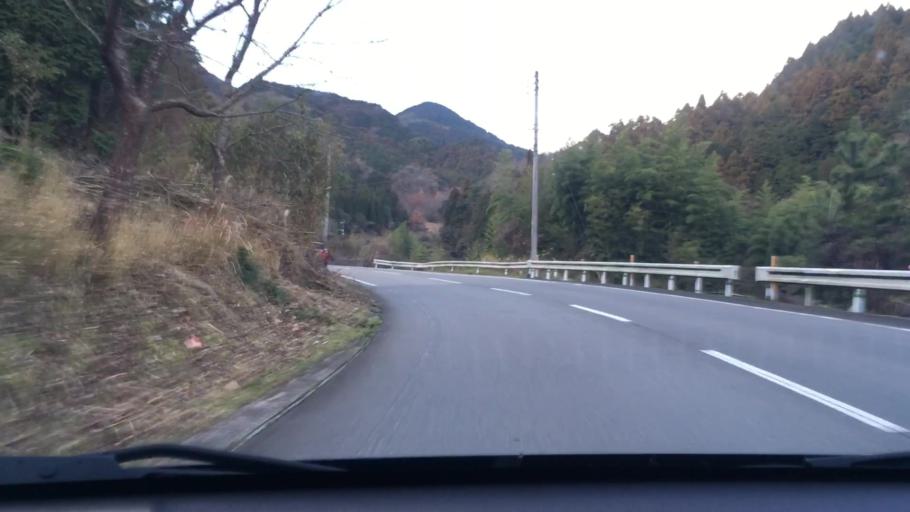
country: JP
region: Oita
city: Bungo-Takada-shi
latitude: 33.4683
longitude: 131.3878
